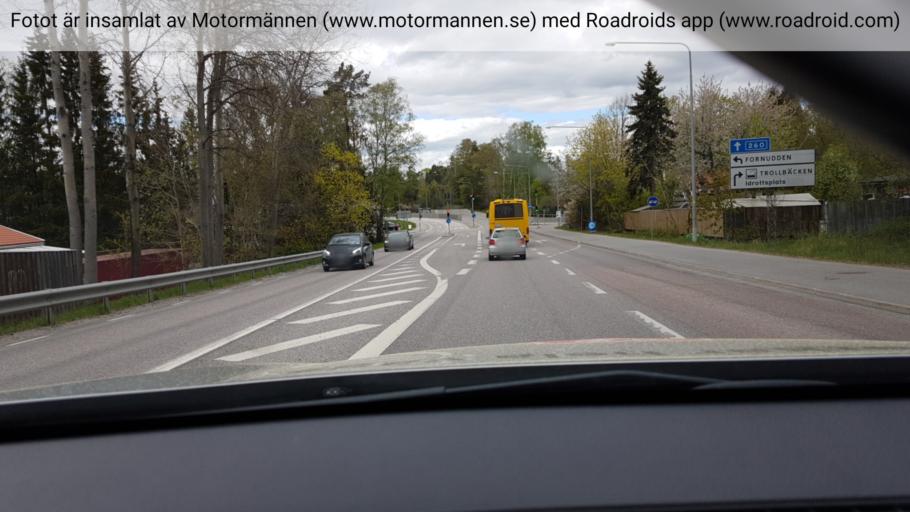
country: SE
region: Stockholm
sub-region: Tyreso Kommun
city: Bollmora
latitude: 59.2268
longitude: 18.2008
